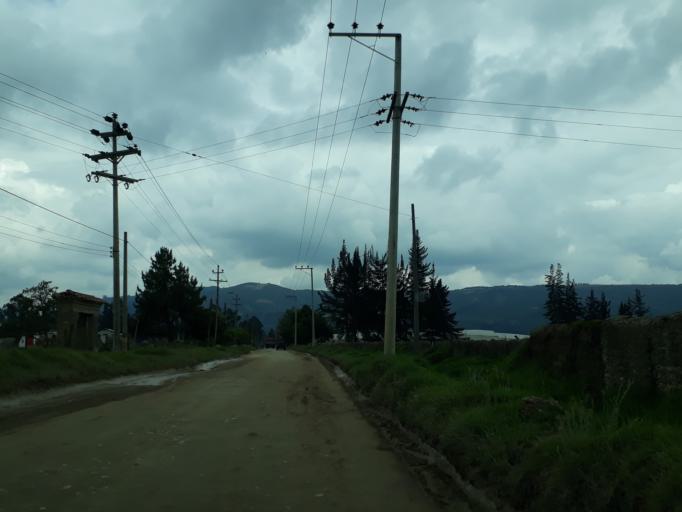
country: CO
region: Cundinamarca
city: Sesquile
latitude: 5.0656
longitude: -73.8086
